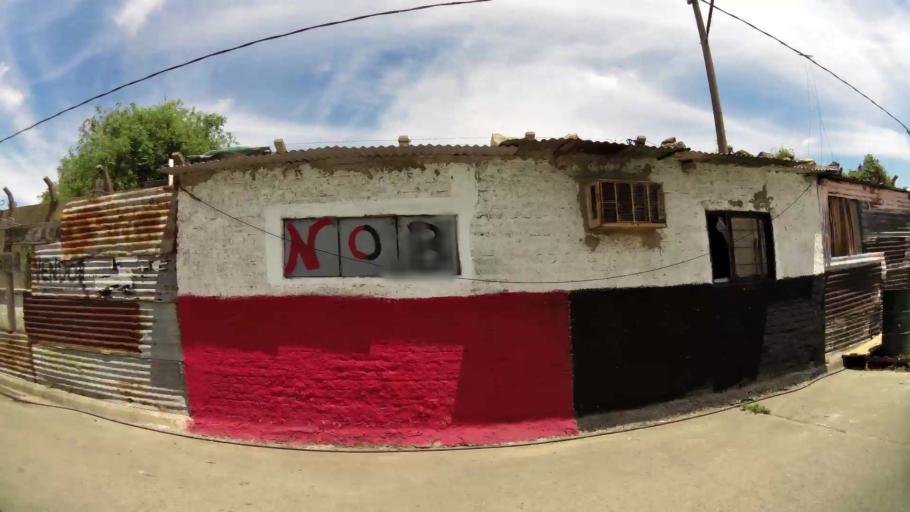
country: AR
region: Santa Fe
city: Gobernador Galvez
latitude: -32.9890
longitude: -60.6229
